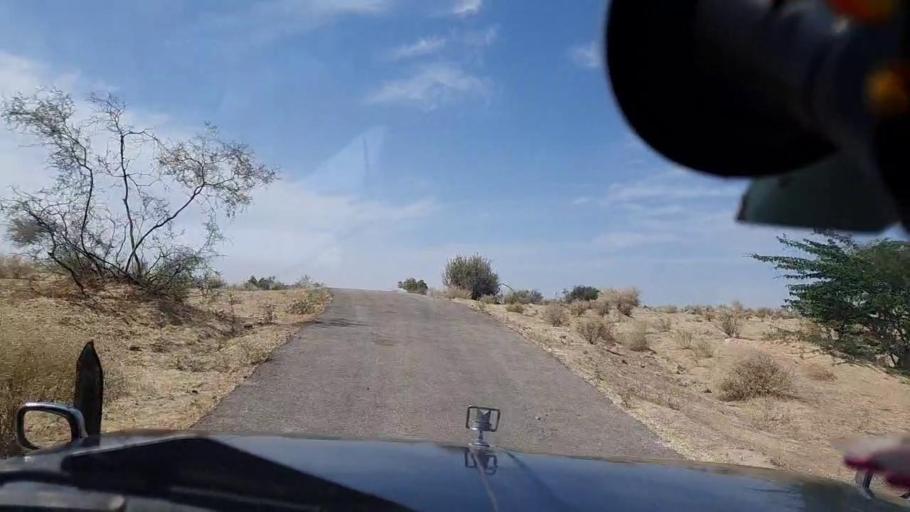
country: PK
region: Sindh
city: Diplo
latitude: 24.3481
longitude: 69.5827
